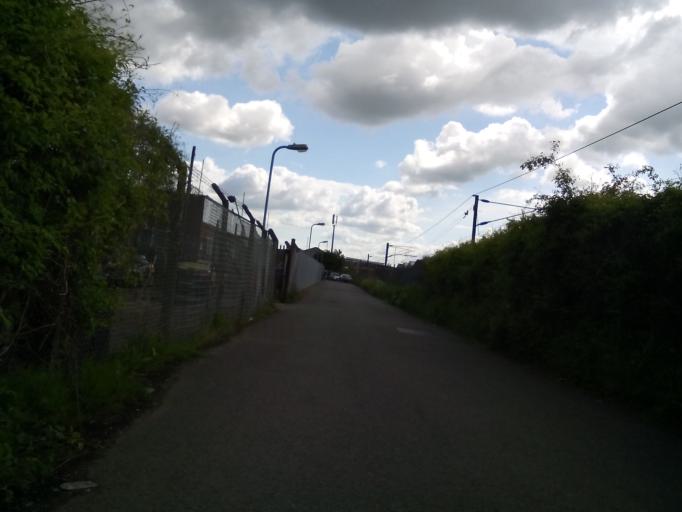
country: GB
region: England
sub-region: Cambridgeshire
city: Cambridge
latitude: 52.2094
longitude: 0.1491
